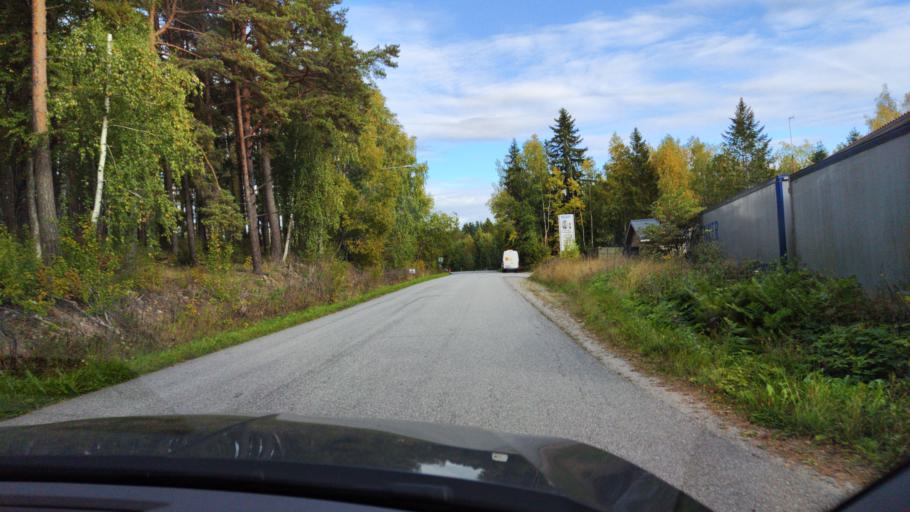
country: FI
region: Varsinais-Suomi
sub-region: Aboland-Turunmaa
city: Laensi-Turunmaa
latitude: 60.2826
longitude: 22.2444
